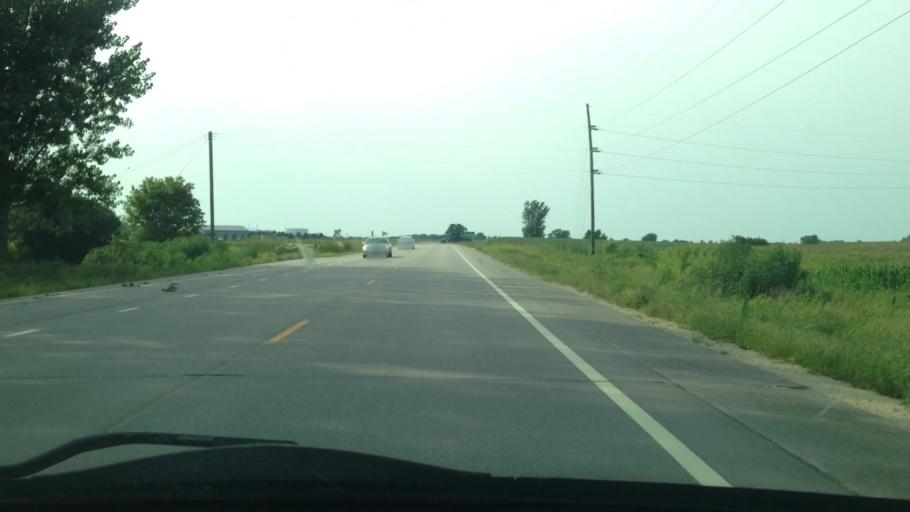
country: US
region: Minnesota
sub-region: Olmsted County
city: Eyota
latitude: 43.9961
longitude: -92.2383
